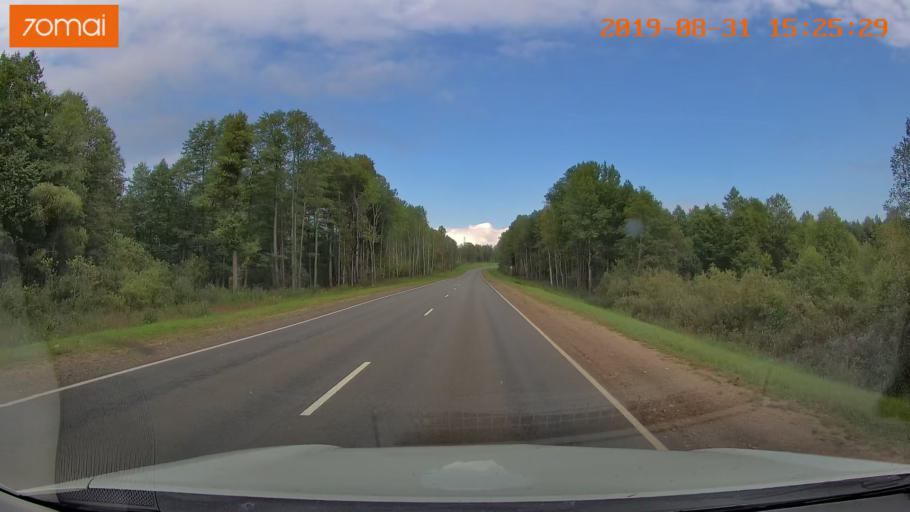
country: RU
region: Kaluga
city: Baryatino
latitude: 54.5421
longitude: 34.5205
